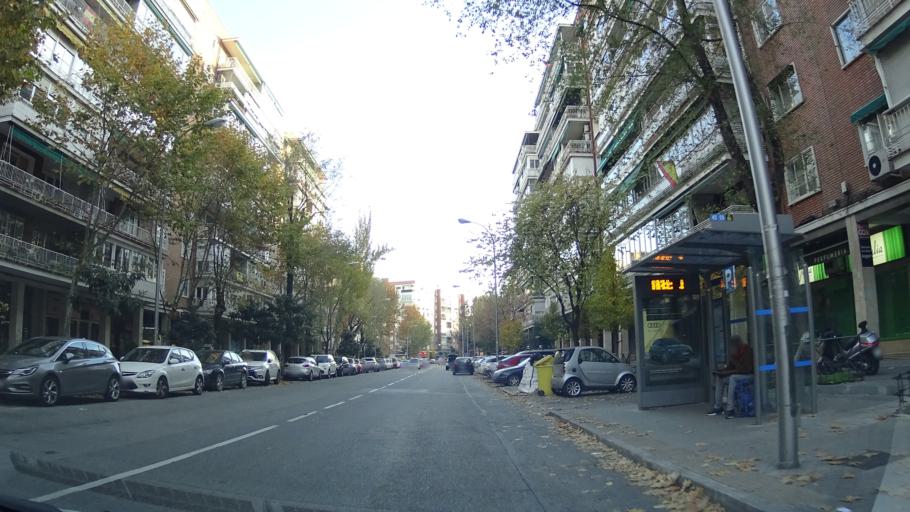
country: ES
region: Madrid
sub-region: Provincia de Madrid
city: Salamanca
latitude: 40.4406
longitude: -3.6630
